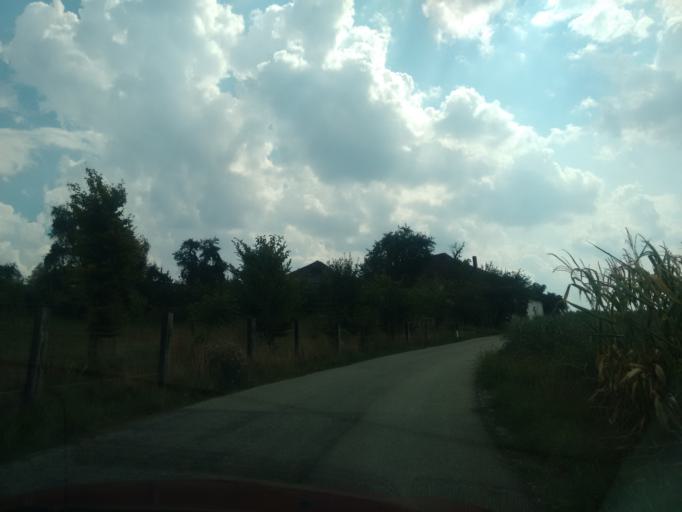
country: AT
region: Upper Austria
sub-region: Politischer Bezirk Grieskirchen
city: Bad Schallerbach
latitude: 48.2521
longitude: 13.9096
